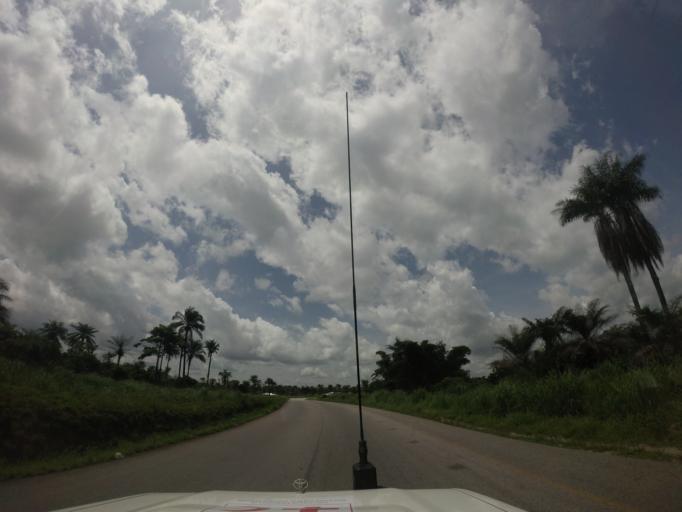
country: SL
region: Northern Province
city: Yonibana
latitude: 8.4829
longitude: -12.4257
